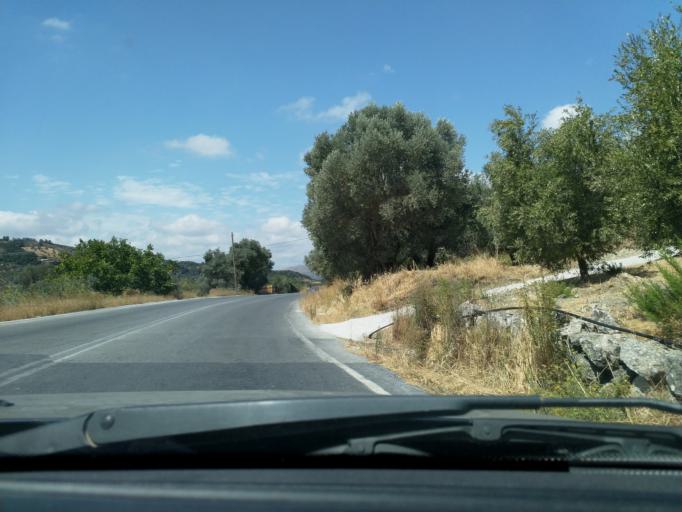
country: GR
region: Crete
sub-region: Nomos Rethymnis
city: Agia Foteini
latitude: 35.1954
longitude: 24.5482
